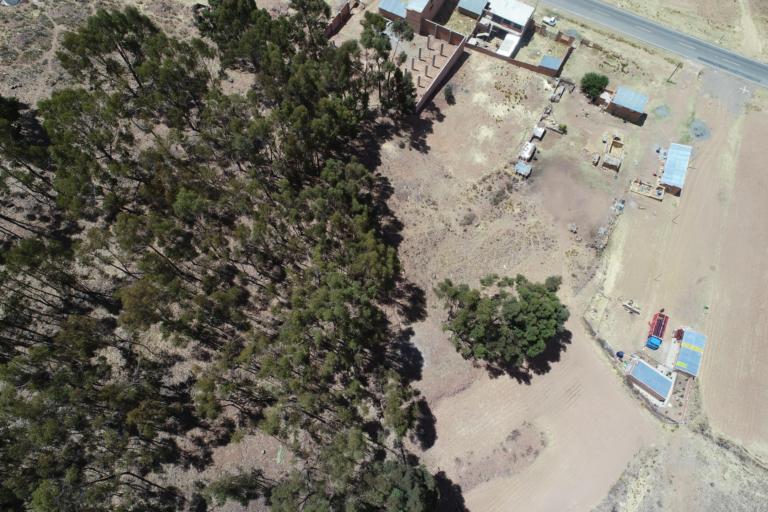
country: BO
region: La Paz
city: Achacachi
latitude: -15.9098
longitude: -68.8862
